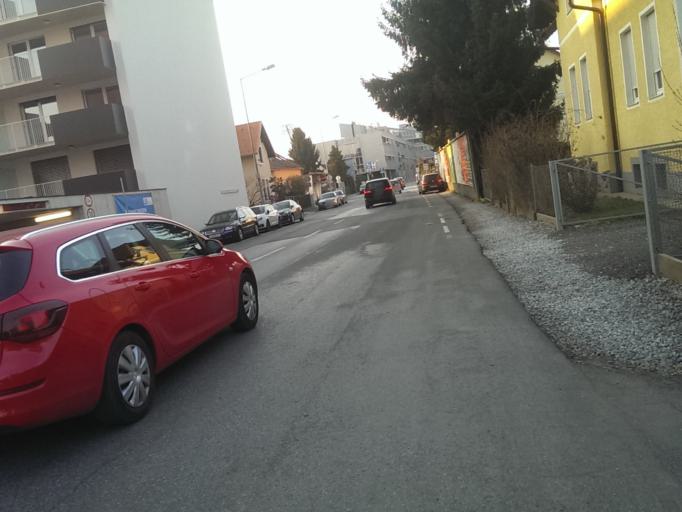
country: AT
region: Styria
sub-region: Graz Stadt
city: Graz
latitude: 47.0449
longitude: 15.4573
